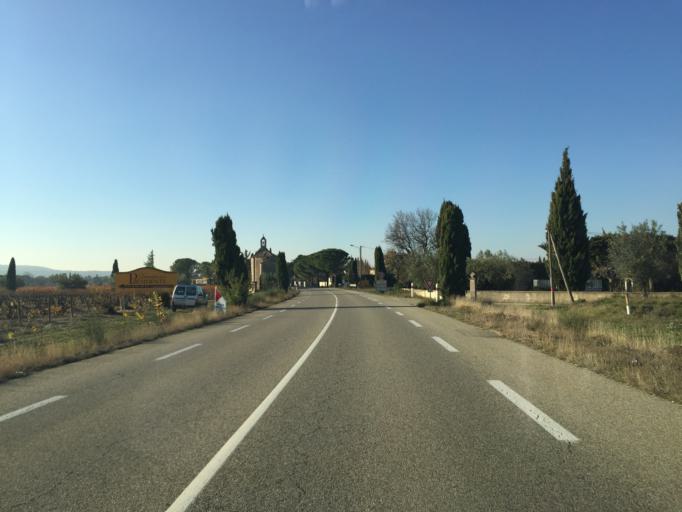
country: FR
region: Provence-Alpes-Cote d'Azur
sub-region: Departement du Vaucluse
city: Sainte-Cecile-les-Vignes
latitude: 44.2421
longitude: 4.8994
